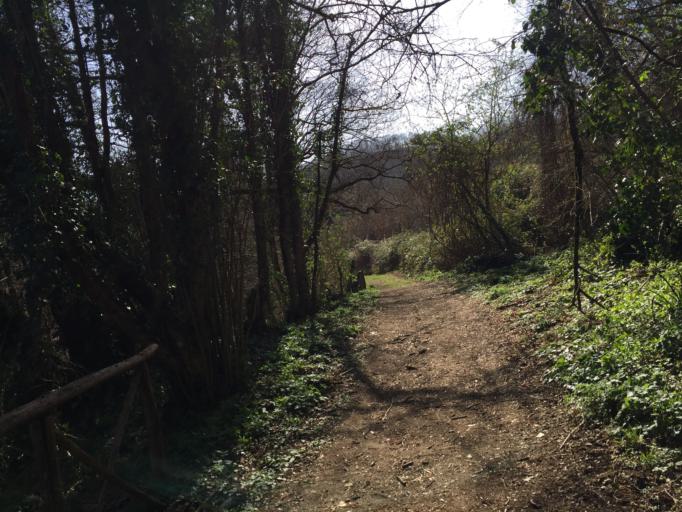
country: IT
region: Latium
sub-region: Provincia di Viterbo
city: Calcata Nuova
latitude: 42.2085
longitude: 12.4147
